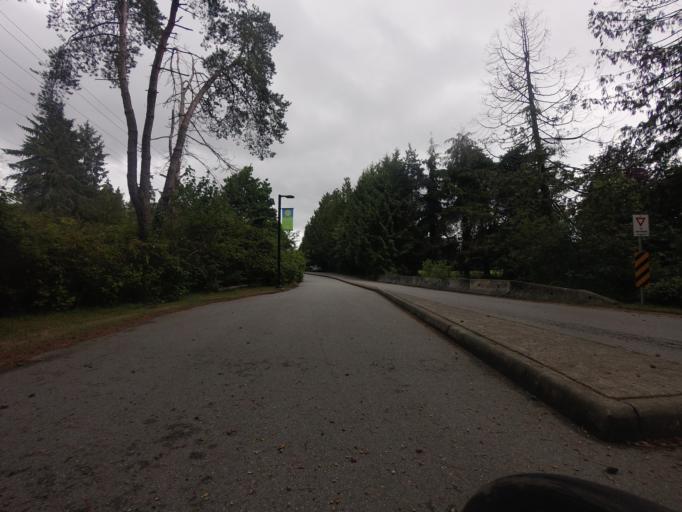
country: CA
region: British Columbia
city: West End
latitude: 49.3242
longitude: -123.1461
